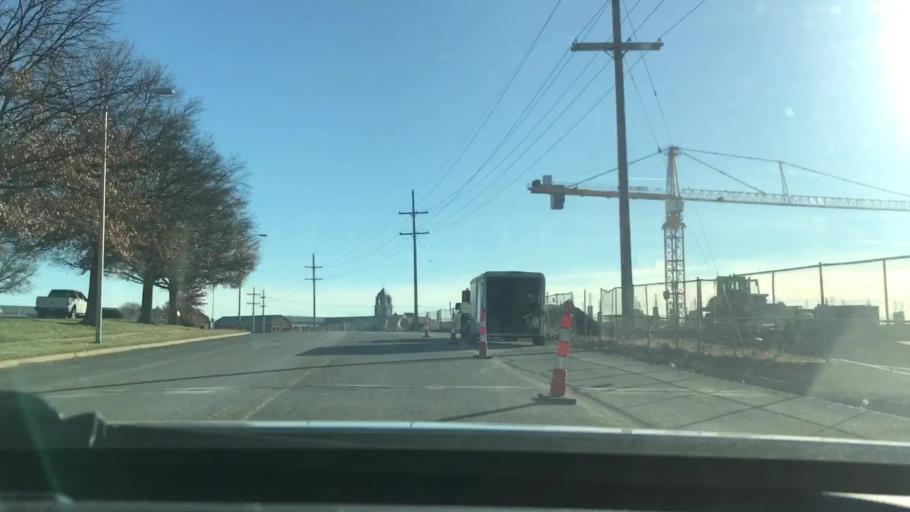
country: US
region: Kansas
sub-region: Johnson County
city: Leawood
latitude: 38.9241
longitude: -94.6583
